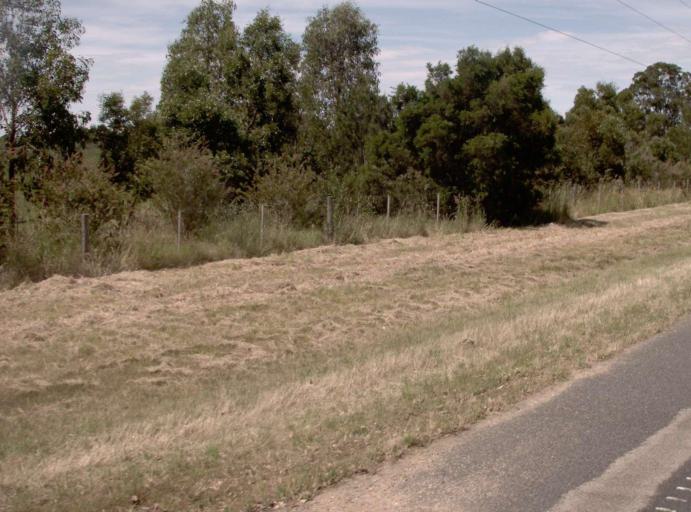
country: AU
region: Victoria
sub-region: Wellington
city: Sale
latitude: -37.9262
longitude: 147.2218
